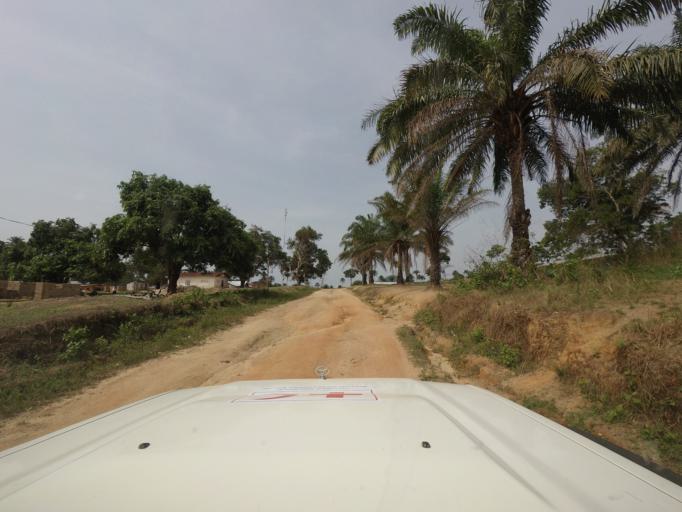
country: GN
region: Nzerekore
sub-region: Macenta
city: Macenta
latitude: 8.4545
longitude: -9.5882
